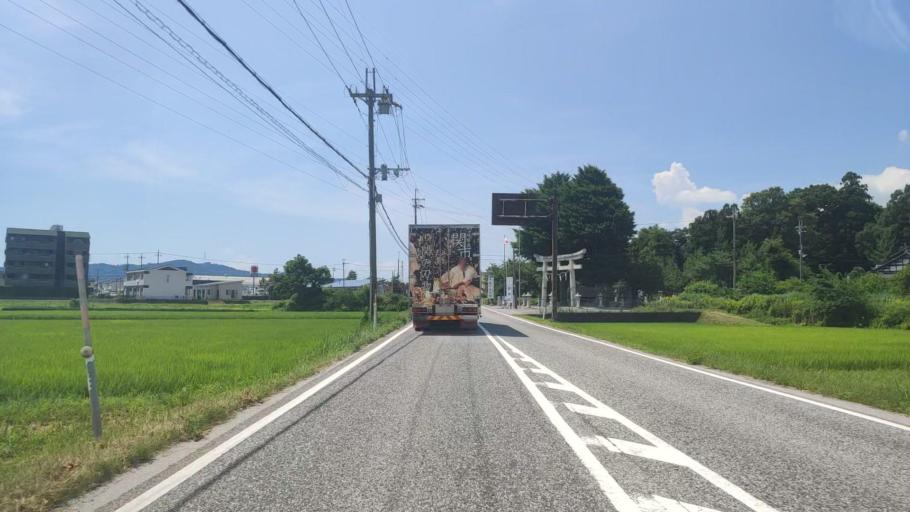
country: JP
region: Shiga Prefecture
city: Nagahama
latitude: 35.3844
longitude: 136.3679
